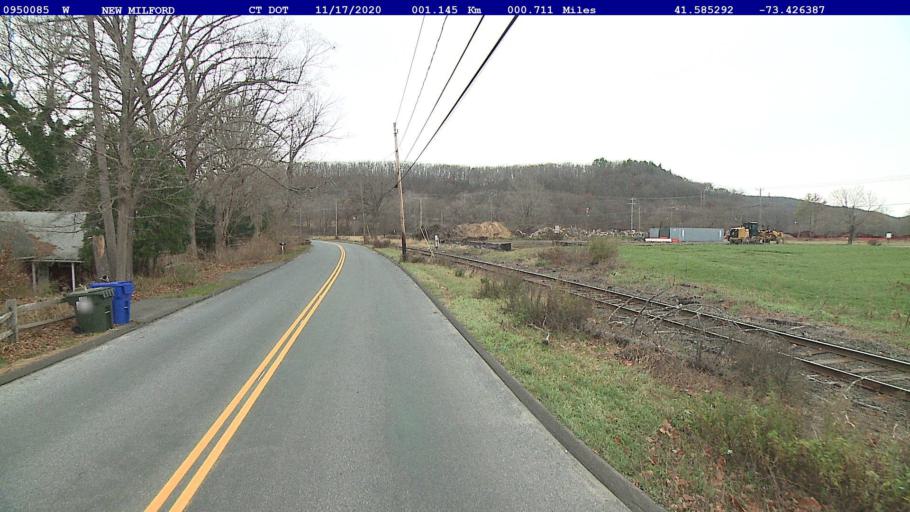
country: US
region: Connecticut
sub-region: Litchfield County
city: New Milford
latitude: 41.5853
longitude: -73.4264
